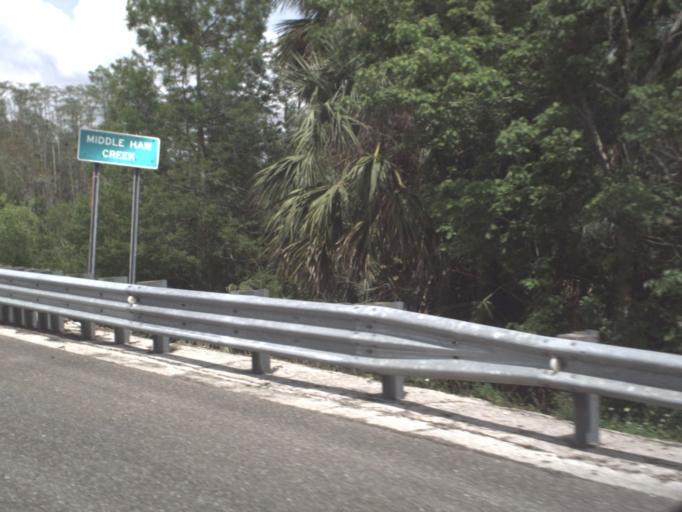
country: US
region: Florida
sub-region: Flagler County
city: Bunnell
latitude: 29.3595
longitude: -81.3114
